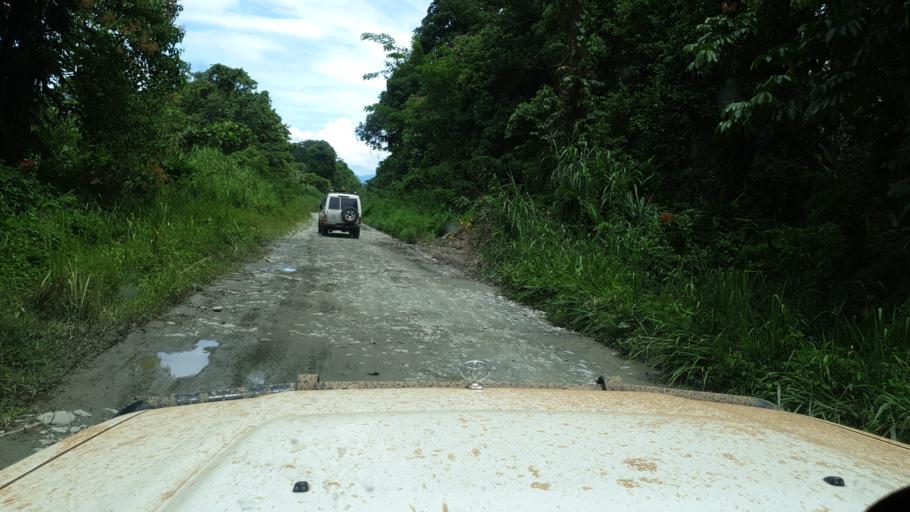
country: PG
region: Northern Province
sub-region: Sohe
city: Kokoda
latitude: -8.9162
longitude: 147.9136
